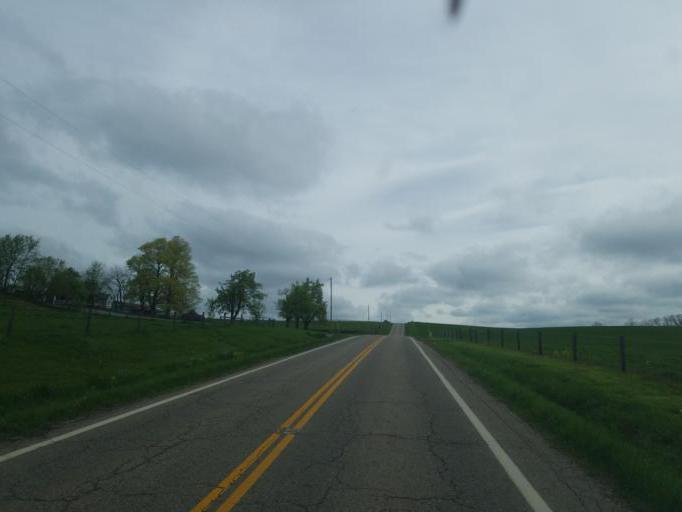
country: US
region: Ohio
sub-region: Ashland County
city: Loudonville
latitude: 40.5547
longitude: -82.1654
